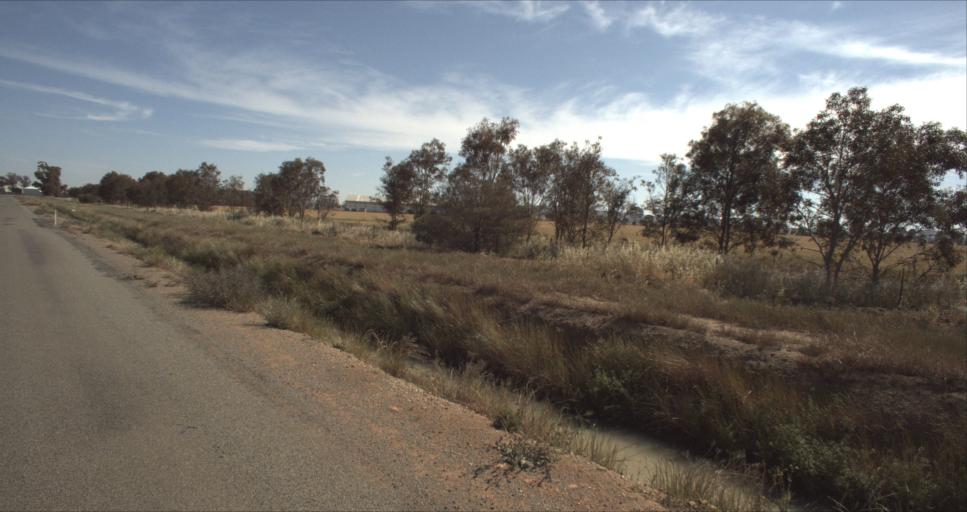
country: AU
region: New South Wales
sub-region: Leeton
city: Leeton
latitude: -34.5632
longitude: 146.4700
